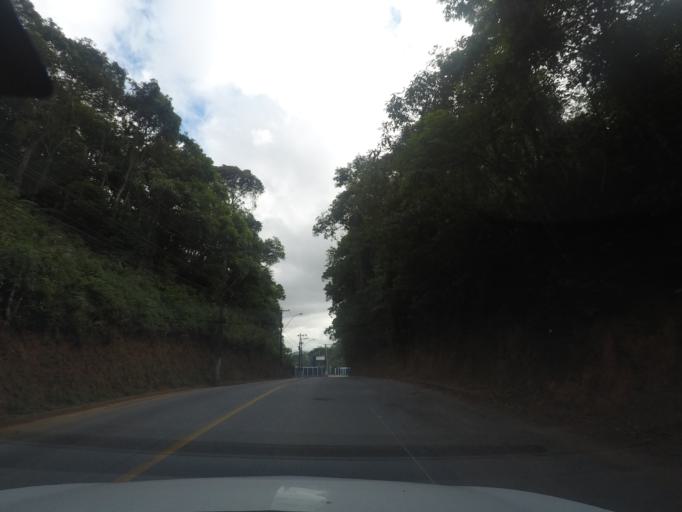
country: BR
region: Rio de Janeiro
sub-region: Teresopolis
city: Teresopolis
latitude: -22.3957
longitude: -42.9600
